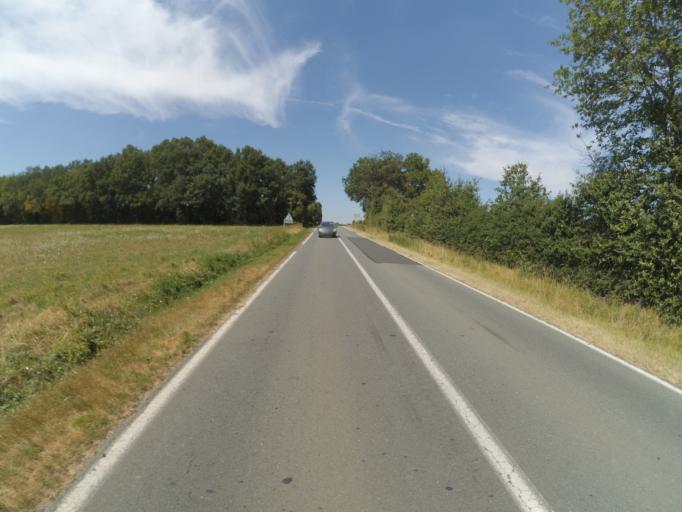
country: FR
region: Poitou-Charentes
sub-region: Departement de la Vienne
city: Saint-Maurice-la-Clouere
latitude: 46.3516
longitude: 0.4486
